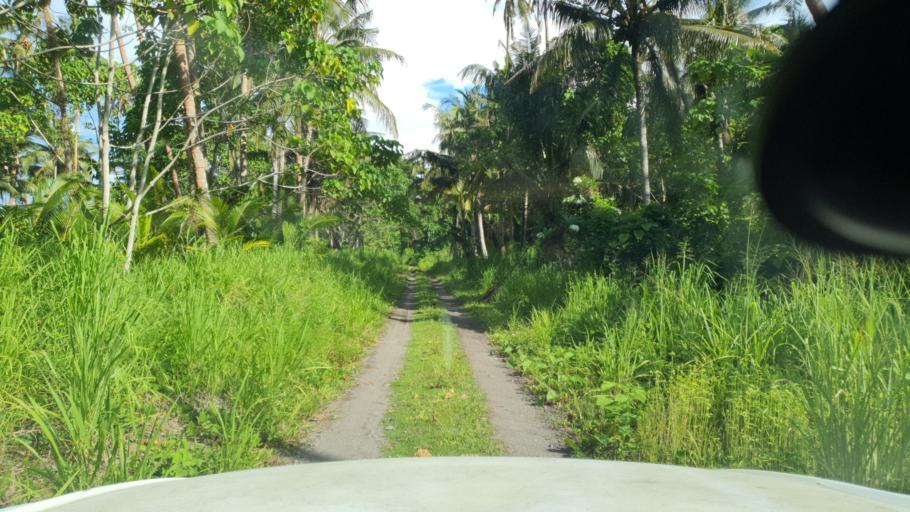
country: SB
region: Guadalcanal
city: Honiara
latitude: -9.2866
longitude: 159.7633
